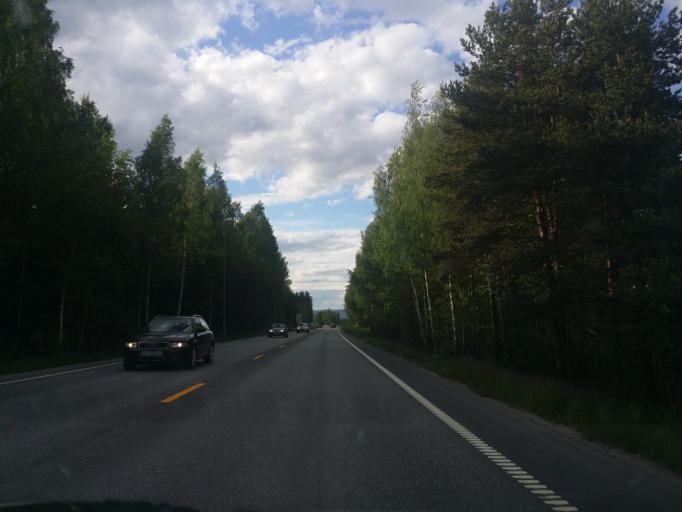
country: NO
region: Hedmark
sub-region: Stange
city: Stange
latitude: 60.7507
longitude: 11.1968
